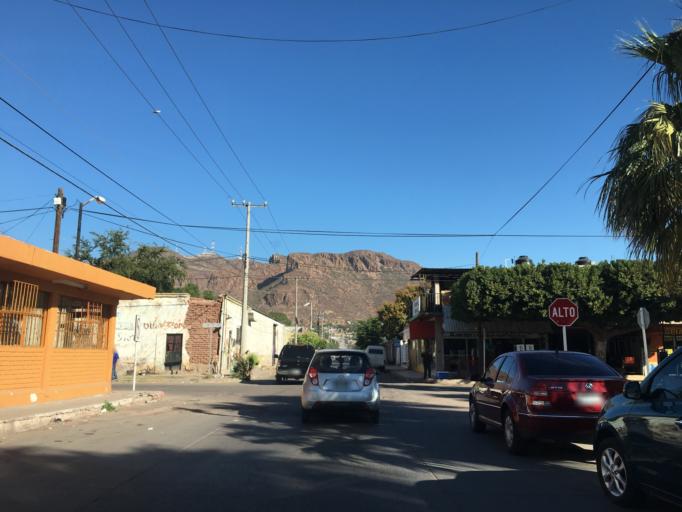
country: MX
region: Sonora
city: Heroica Guaymas
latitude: 27.9182
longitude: -110.8953
